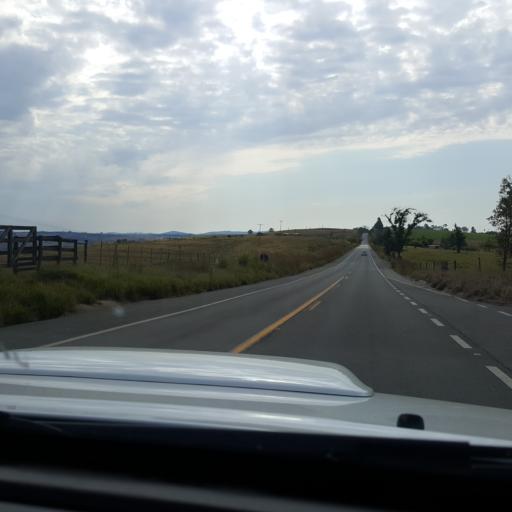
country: BR
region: Sao Paulo
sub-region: Itaporanga
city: Itaporanga
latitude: -23.7608
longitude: -49.4490
